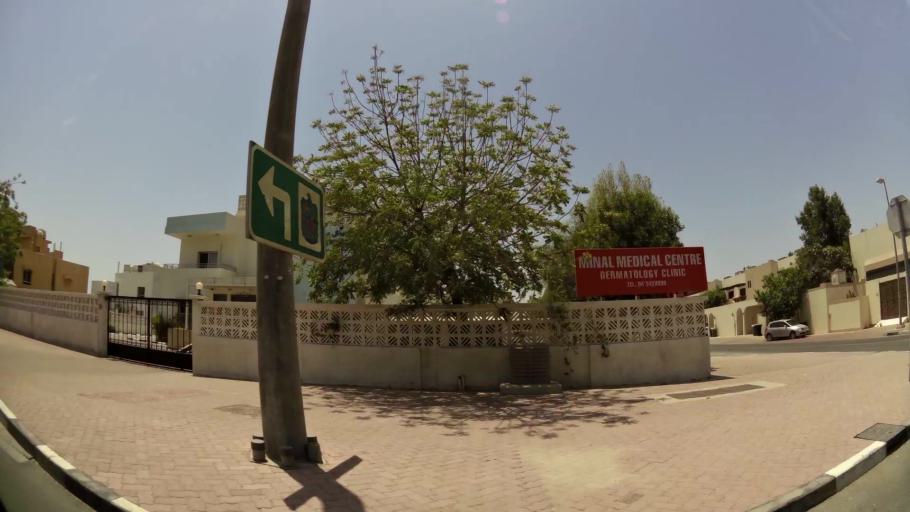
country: AE
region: Dubai
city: Dubai
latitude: 25.2137
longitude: 55.2581
